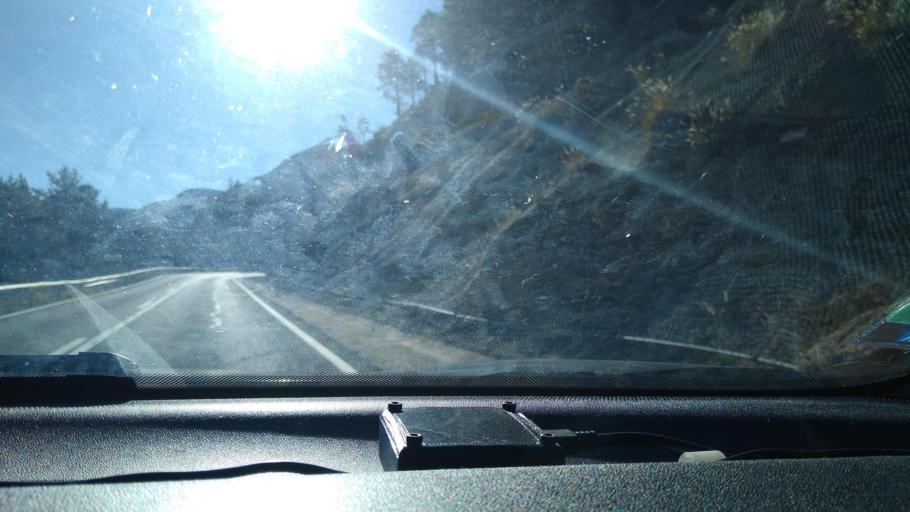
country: ES
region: Catalonia
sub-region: Provincia de Barcelona
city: Saldes
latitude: 42.2193
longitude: 1.7190
